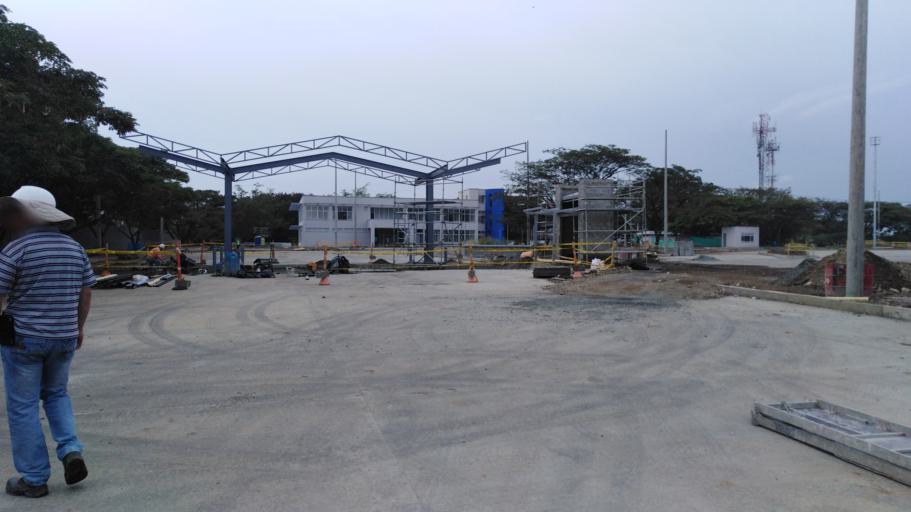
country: CO
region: Valle del Cauca
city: Cali
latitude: 3.3603
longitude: -76.5207
